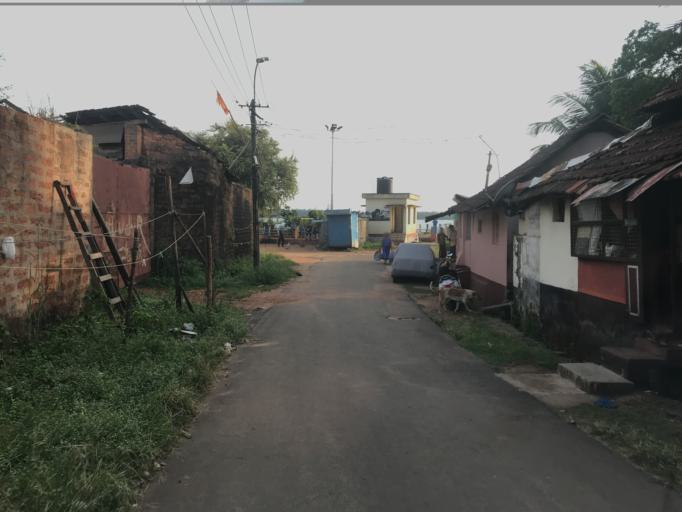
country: IN
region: Karnataka
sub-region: Dakshina Kannada
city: Ullal
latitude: 12.8439
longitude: 74.8425
